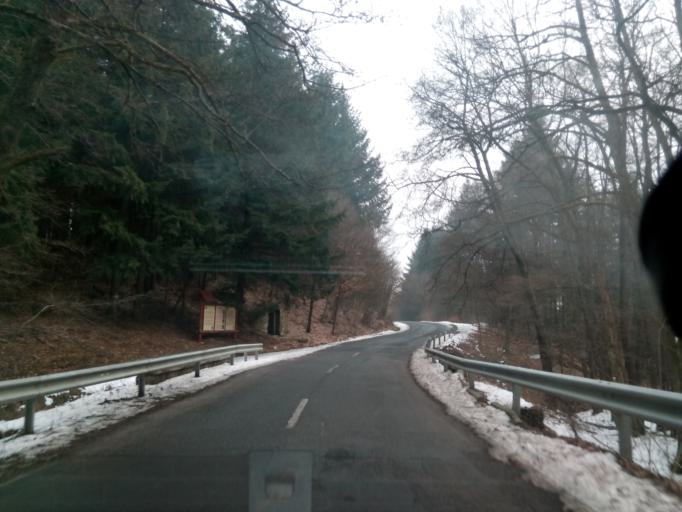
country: HU
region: Borsod-Abauj-Zemplen
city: Gonc
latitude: 48.4887
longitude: 21.4034
